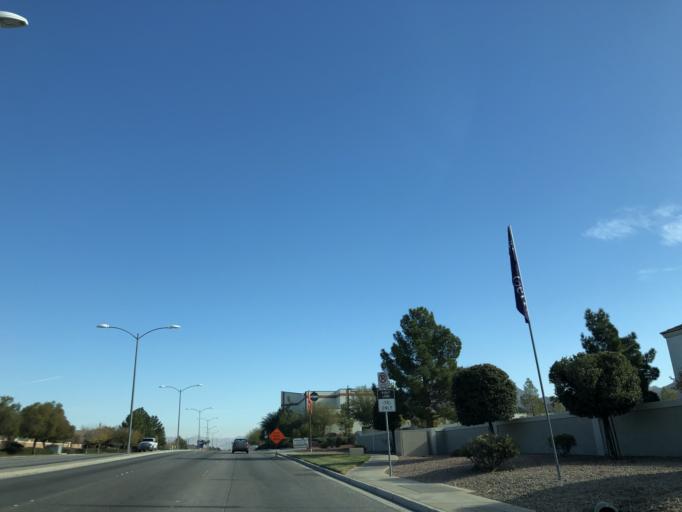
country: US
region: Nevada
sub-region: Clark County
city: Whitney
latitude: 36.0219
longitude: -115.0449
